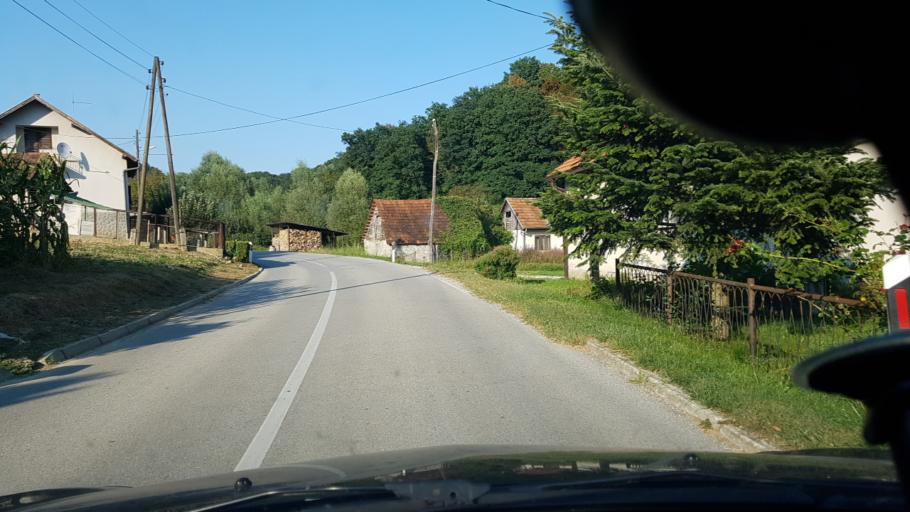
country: SI
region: Bistrica ob Sotli
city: Bistrica ob Sotli
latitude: 46.0504
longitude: 15.7687
